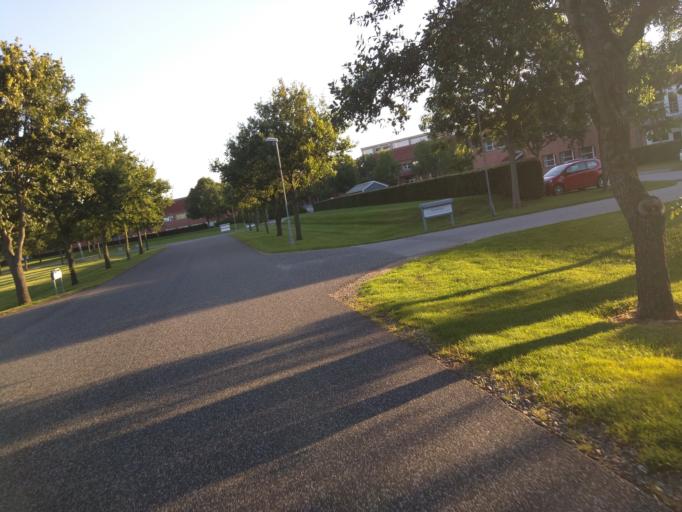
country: DK
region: Central Jutland
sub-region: Viborg Kommune
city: Bjerringbro
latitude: 56.4872
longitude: 9.5822
